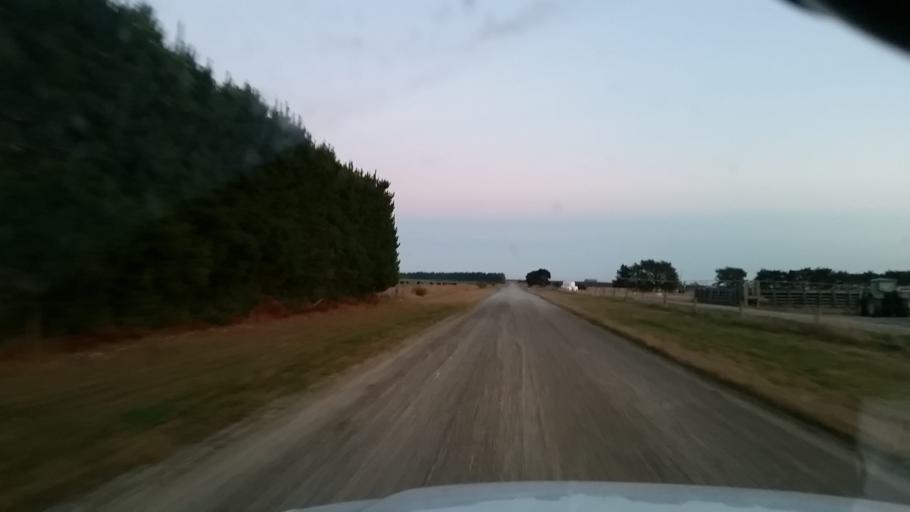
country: NZ
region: Canterbury
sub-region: Ashburton District
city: Tinwald
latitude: -43.9332
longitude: 171.6077
